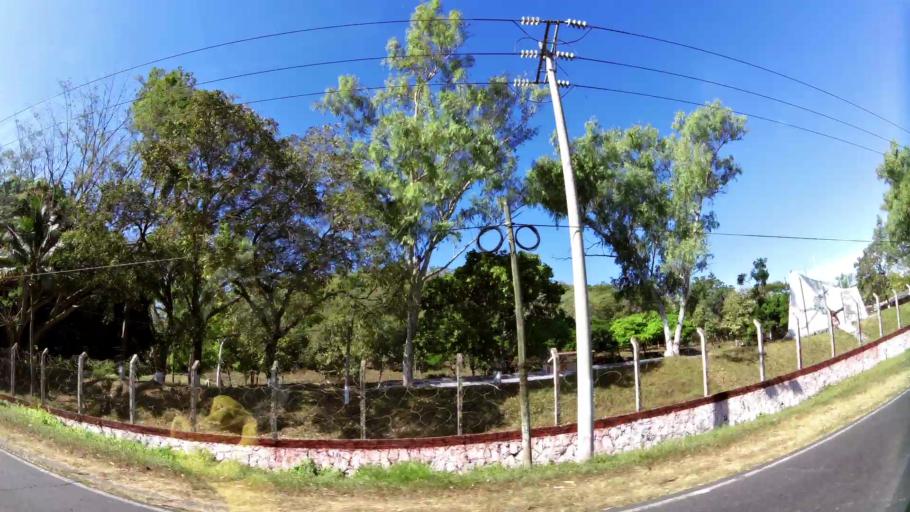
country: SV
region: La Libertad
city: San Juan Opico
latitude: 13.8384
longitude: -89.3598
